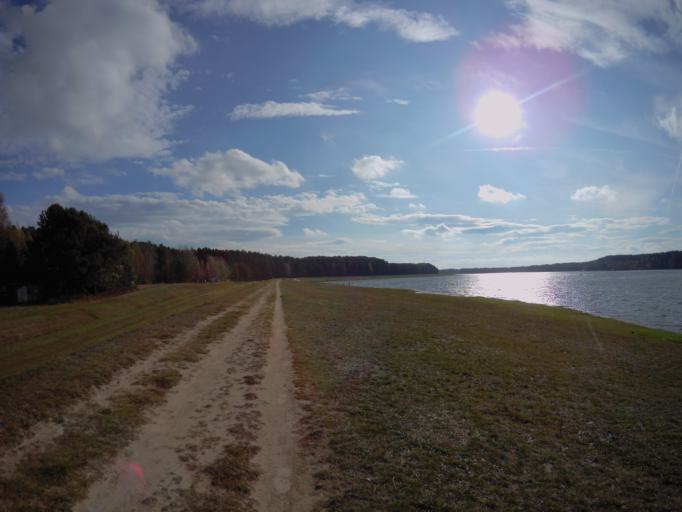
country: PL
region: Subcarpathian Voivodeship
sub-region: Powiat kolbuszowski
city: Lipnica
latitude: 50.3371
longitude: 21.9424
